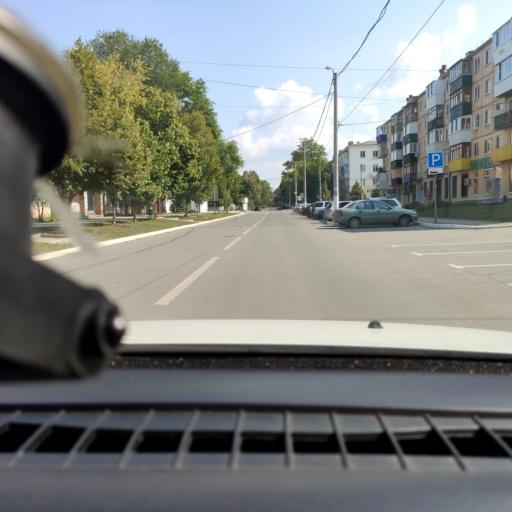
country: RU
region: Samara
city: Chapayevsk
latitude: 52.9783
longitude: 49.7112
